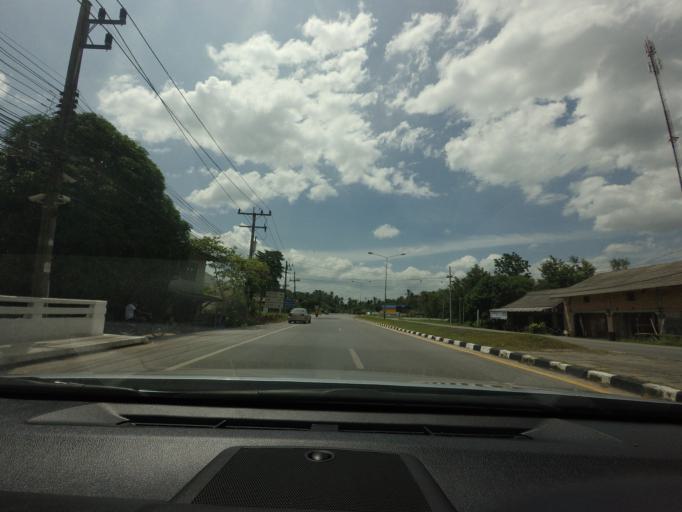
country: TH
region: Yala
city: Raman
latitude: 6.4567
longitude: 101.3463
